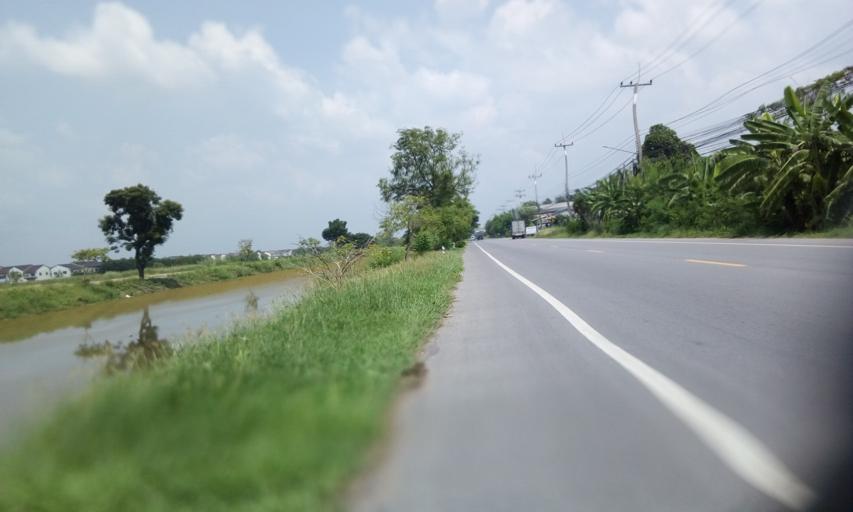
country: TH
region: Pathum Thani
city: Nong Suea
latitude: 14.0617
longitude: 100.8243
